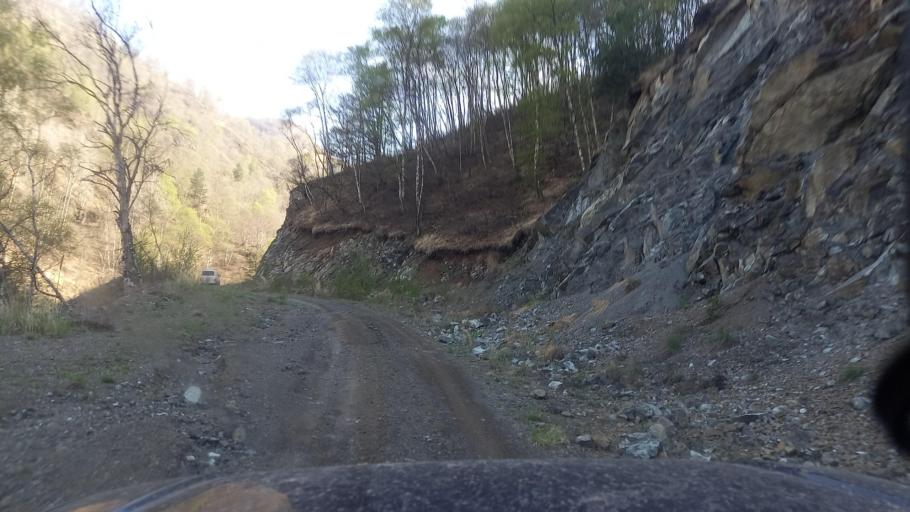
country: RU
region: Kabardino-Balkariya
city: Kamennomostskoye
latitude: 43.7084
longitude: 42.8459
